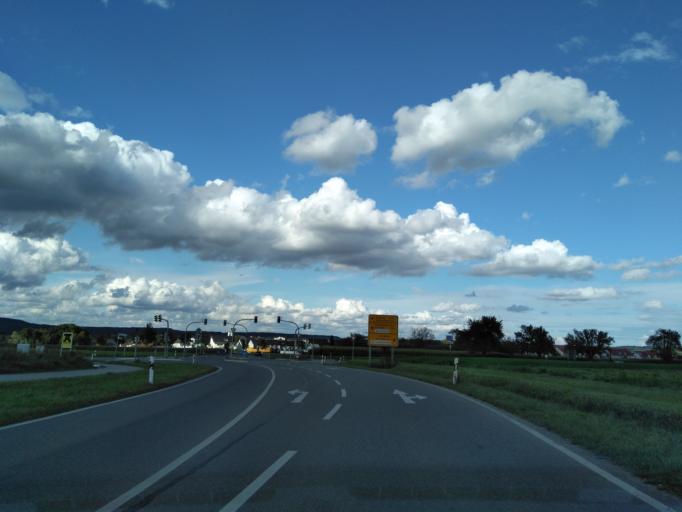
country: DE
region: Baden-Wuerttemberg
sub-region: Regierungsbezirk Stuttgart
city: Oberriexingen
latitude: 48.9505
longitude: 9.0566
